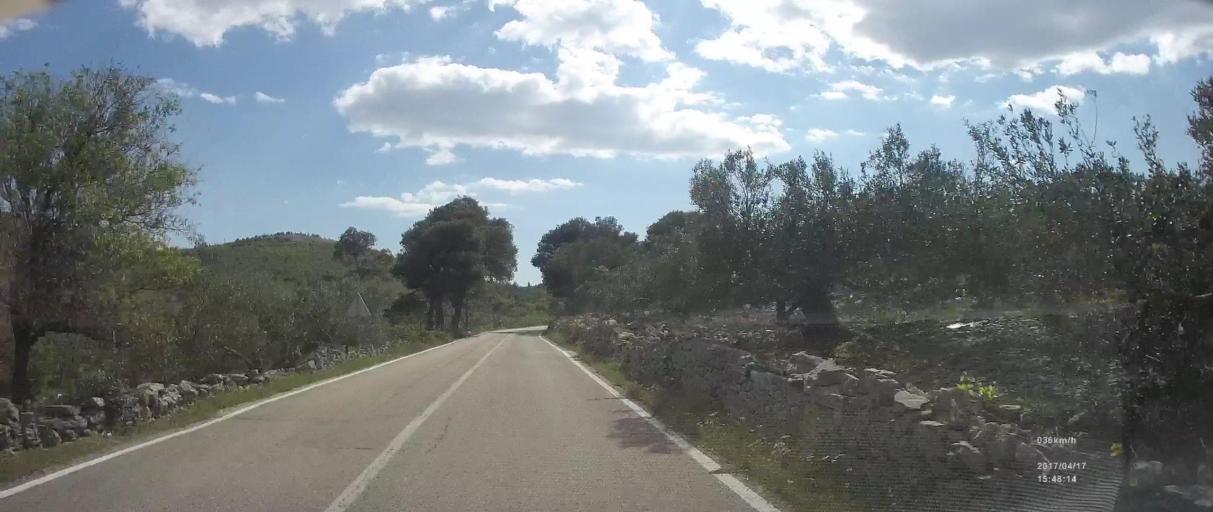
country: HR
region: Sibensko-Kniniska
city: Primosten
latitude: 43.6212
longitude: 15.9827
